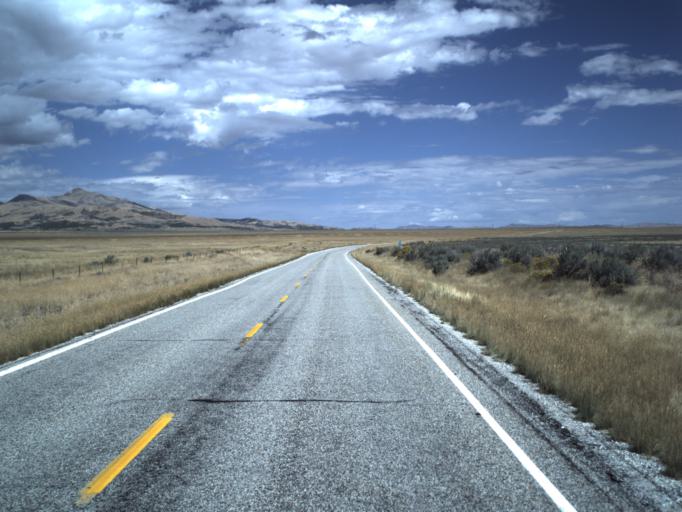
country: US
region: Idaho
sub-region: Oneida County
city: Malad City
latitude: 41.9452
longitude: -113.0815
